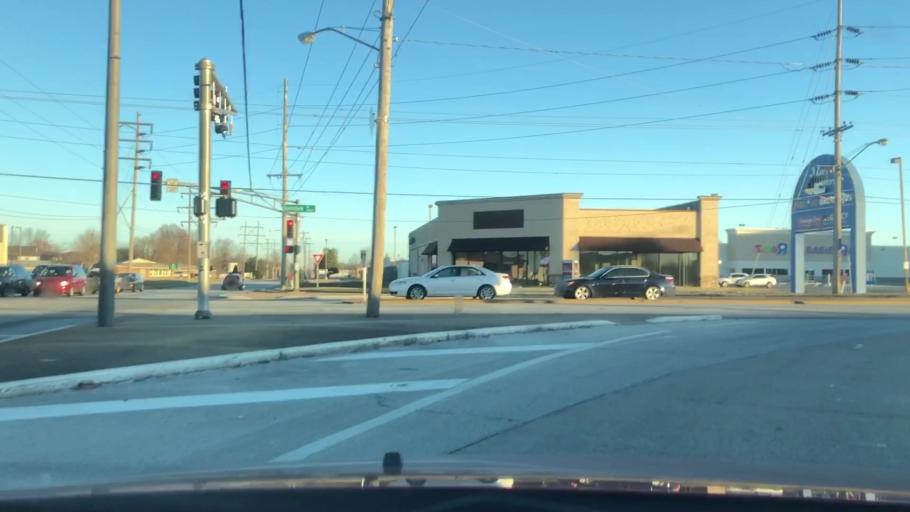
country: US
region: Missouri
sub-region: Greene County
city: Springfield
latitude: 37.1593
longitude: -93.2716
